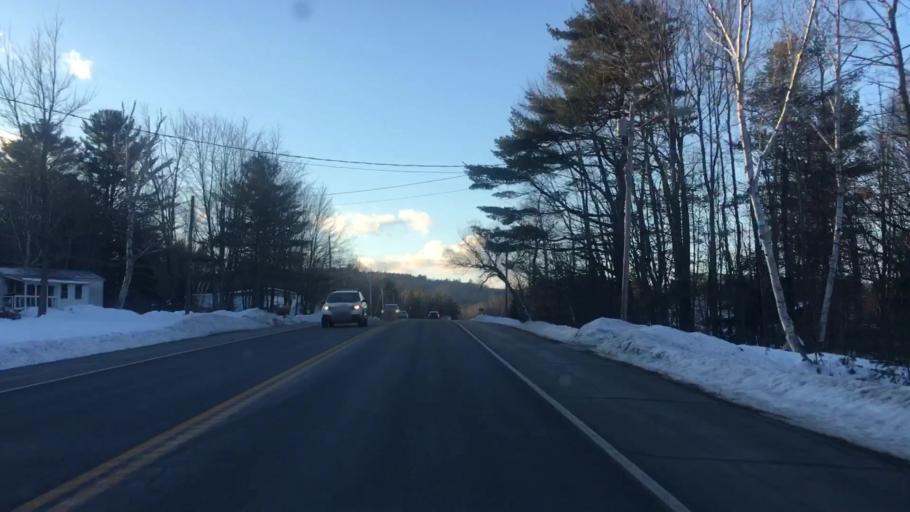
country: US
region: Maine
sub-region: Franklin County
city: Wilton
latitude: 44.5842
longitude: -70.2417
